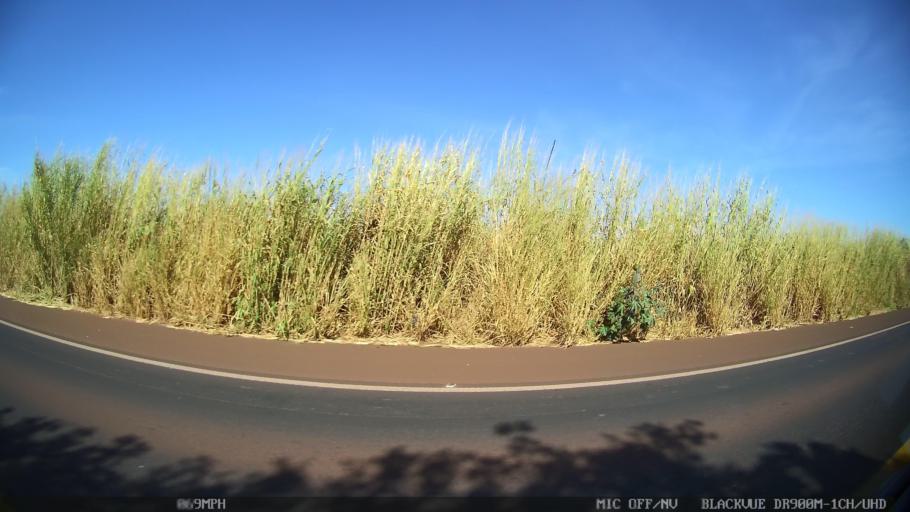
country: BR
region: Sao Paulo
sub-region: Barretos
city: Barretos
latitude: -20.4838
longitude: -48.5095
